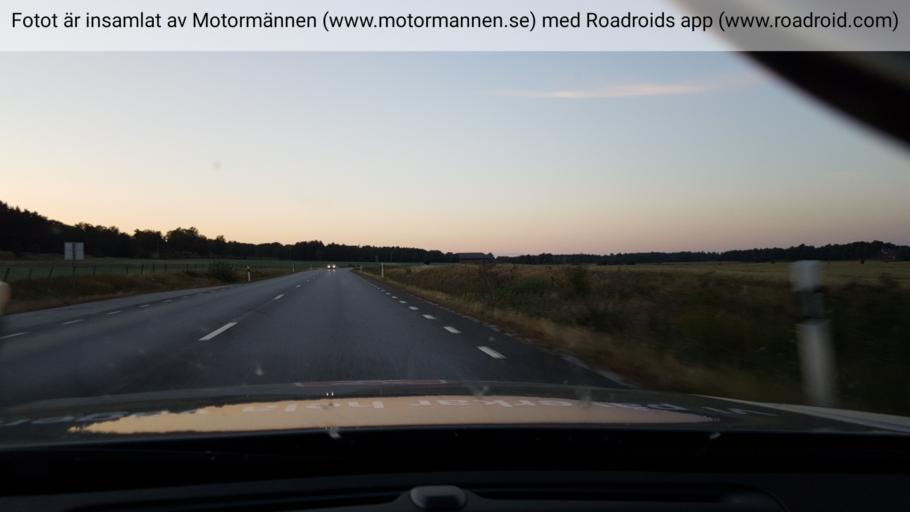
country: SE
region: Vaestra Goetaland
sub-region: Mariestads Kommun
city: Mariestad
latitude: 58.7610
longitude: 13.9472
